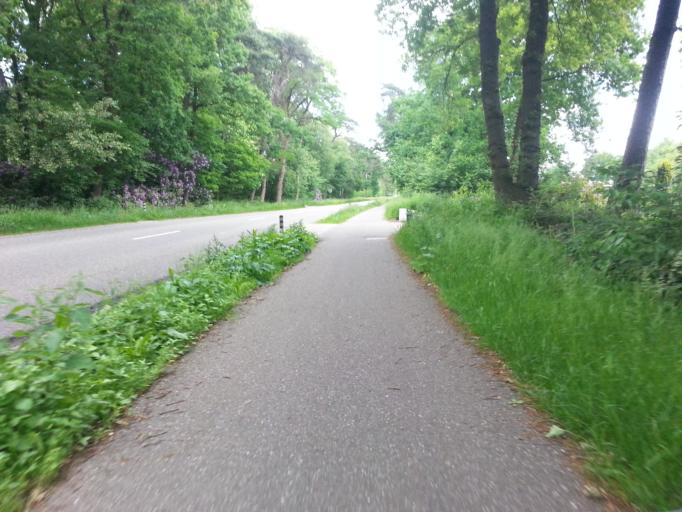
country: NL
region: Gelderland
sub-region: Gemeente Ede
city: Ederveen
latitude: 52.0960
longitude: 5.5435
